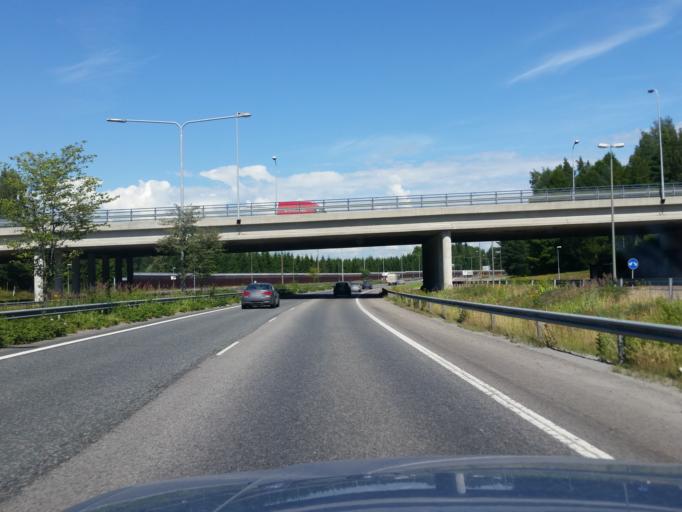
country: FI
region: Uusimaa
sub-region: Helsinki
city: Helsinki
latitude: 60.2290
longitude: 24.9435
